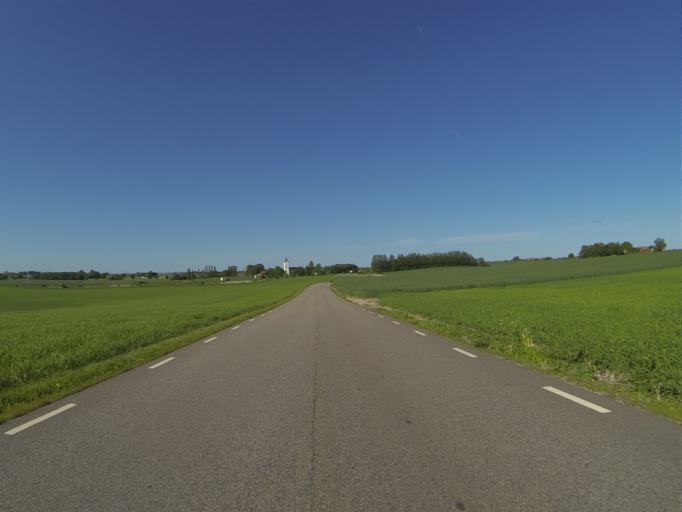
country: SE
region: Skane
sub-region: Staffanstorps Kommun
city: Hjaerup
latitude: 55.6163
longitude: 13.1549
